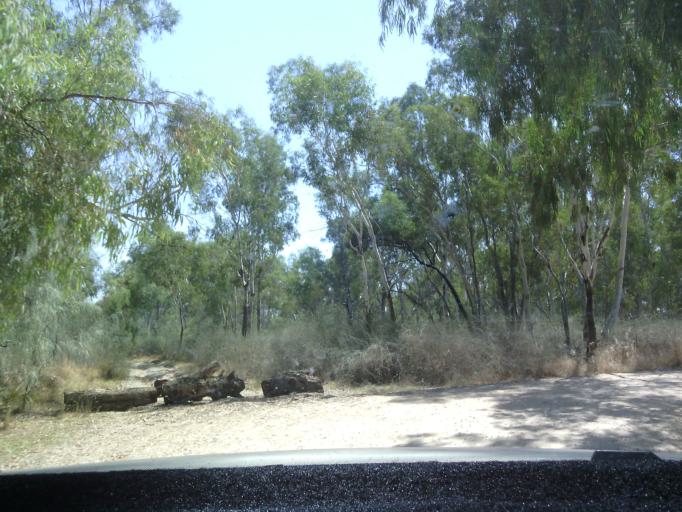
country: AU
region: South Australia
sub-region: Renmark Paringa
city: Renmark
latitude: -34.2159
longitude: 140.7381
